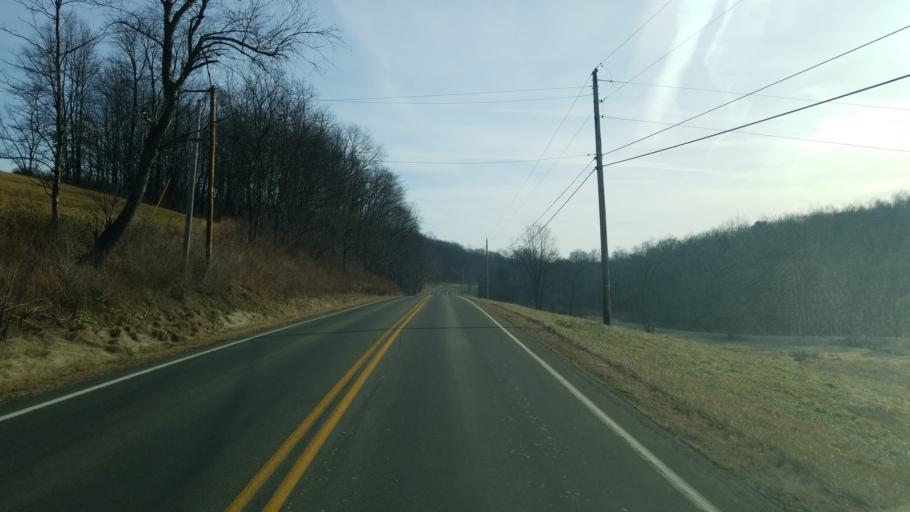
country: US
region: Pennsylvania
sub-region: Indiana County
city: Chevy Chase Heights
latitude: 40.7589
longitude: -79.1299
